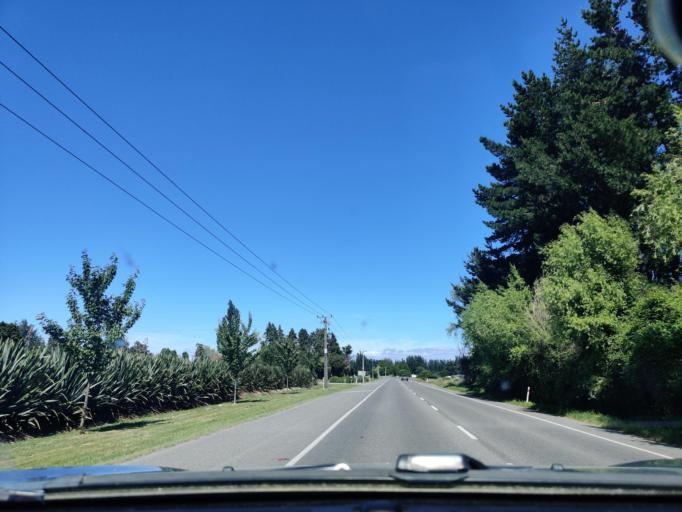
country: NZ
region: Wellington
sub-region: Masterton District
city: Masterton
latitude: -41.0667
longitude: 175.4796
